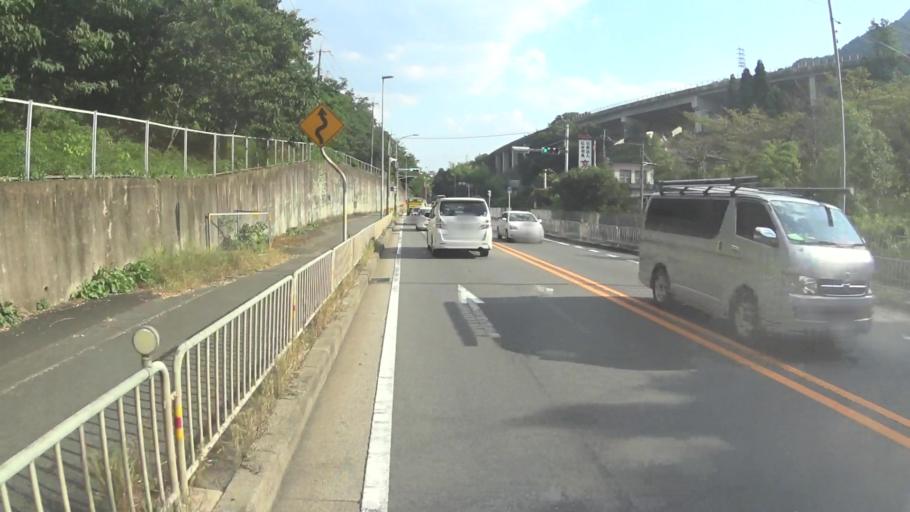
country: JP
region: Kyoto
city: Muko
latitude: 34.9841
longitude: 135.6541
